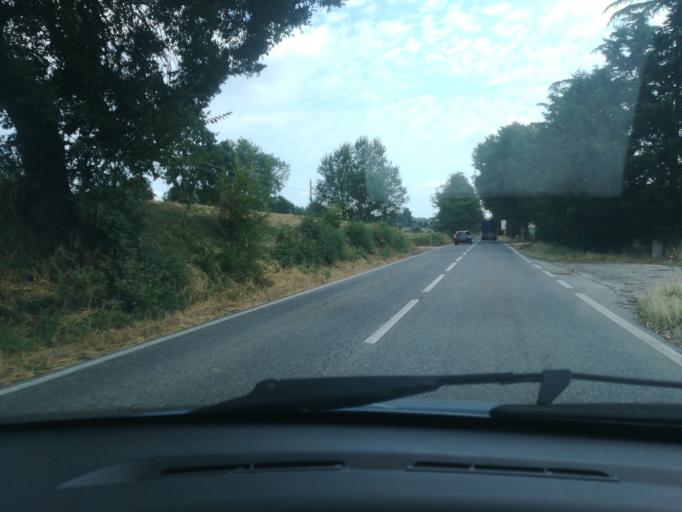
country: IT
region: The Marches
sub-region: Provincia di Macerata
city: Recanati
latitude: 43.3768
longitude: 13.5290
